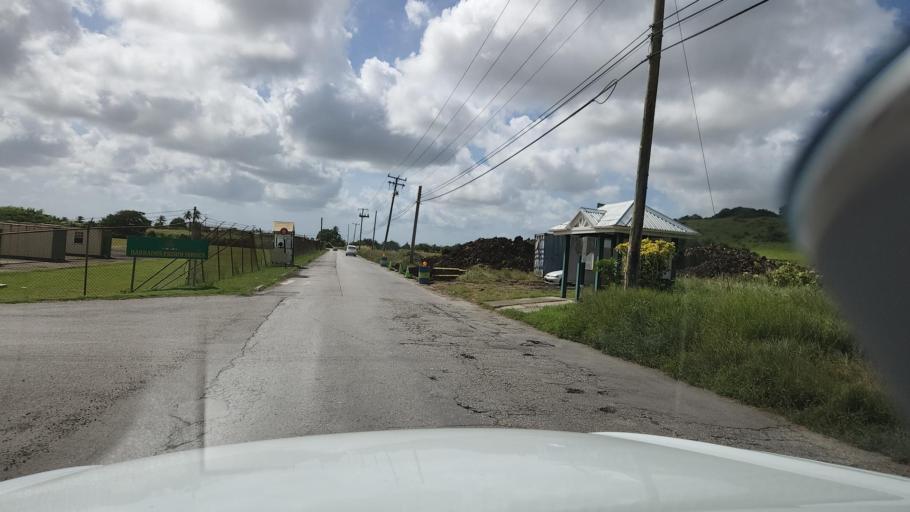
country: BB
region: Saint John
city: Four Cross Roads
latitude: 13.1437
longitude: -59.4827
